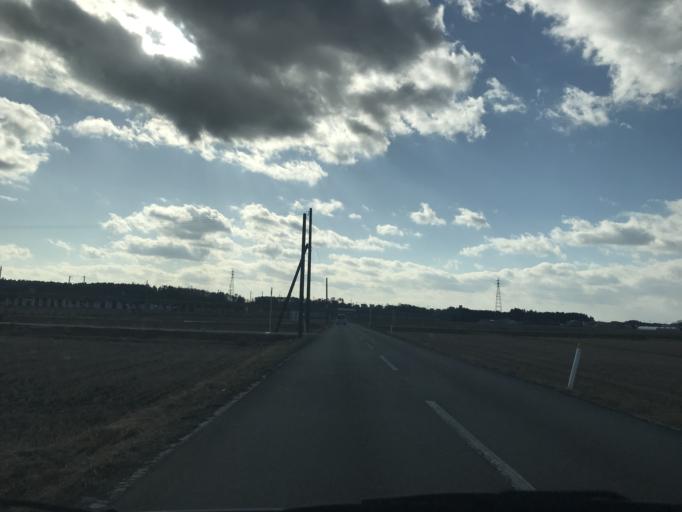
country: JP
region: Iwate
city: Ichinoseki
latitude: 38.7450
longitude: 141.0664
